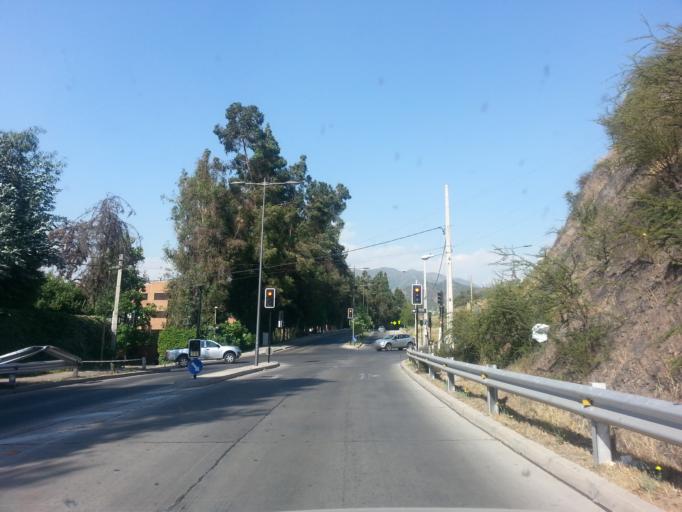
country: CL
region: Santiago Metropolitan
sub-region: Provincia de Santiago
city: Villa Presidente Frei, Nunoa, Santiago, Chile
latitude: -33.3814
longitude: -70.5128
